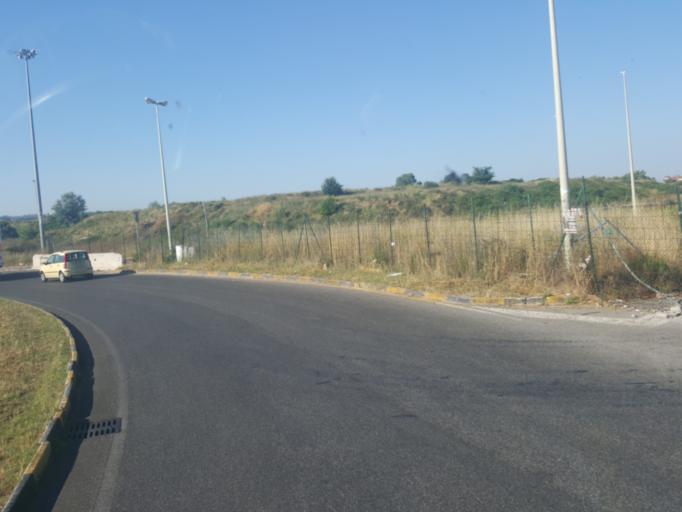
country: IT
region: Latium
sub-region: Citta metropolitana di Roma Capitale
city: Frascati
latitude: 41.8425
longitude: 12.6416
